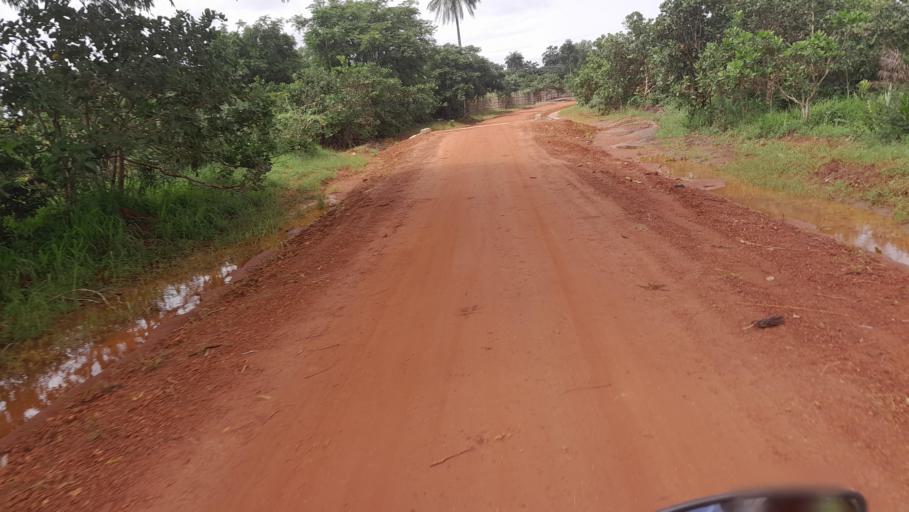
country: GN
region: Boke
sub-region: Boffa
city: Boffa
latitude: 10.0675
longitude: -13.8675
